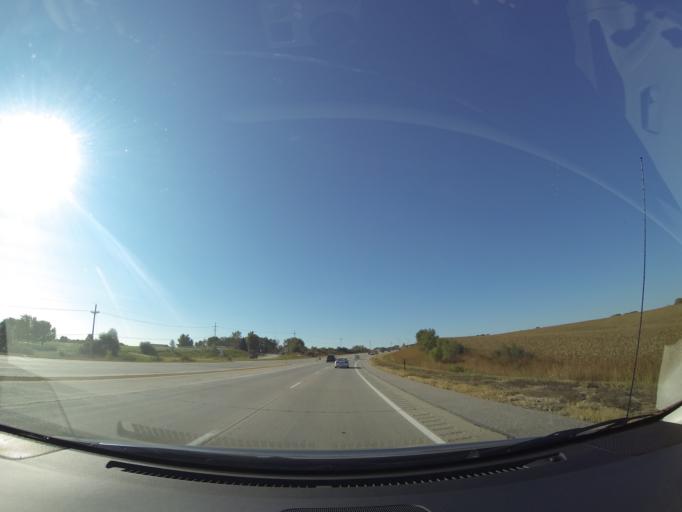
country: US
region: Nebraska
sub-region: Sarpy County
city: Gretna
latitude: 41.1577
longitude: -96.2343
